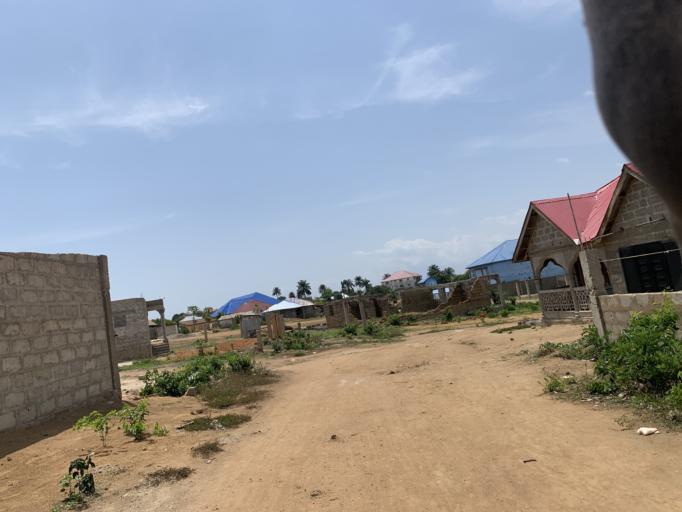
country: SL
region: Western Area
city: Waterloo
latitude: 8.3409
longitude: -13.0363
